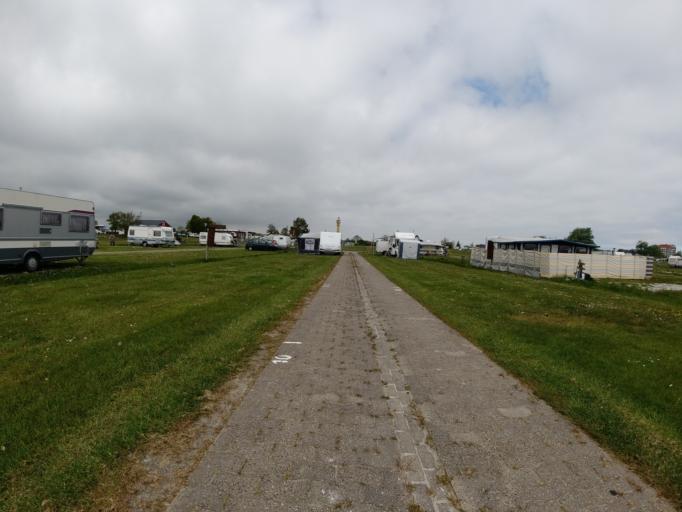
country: DE
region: Lower Saxony
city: Schillig
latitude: 53.6987
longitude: 8.0266
